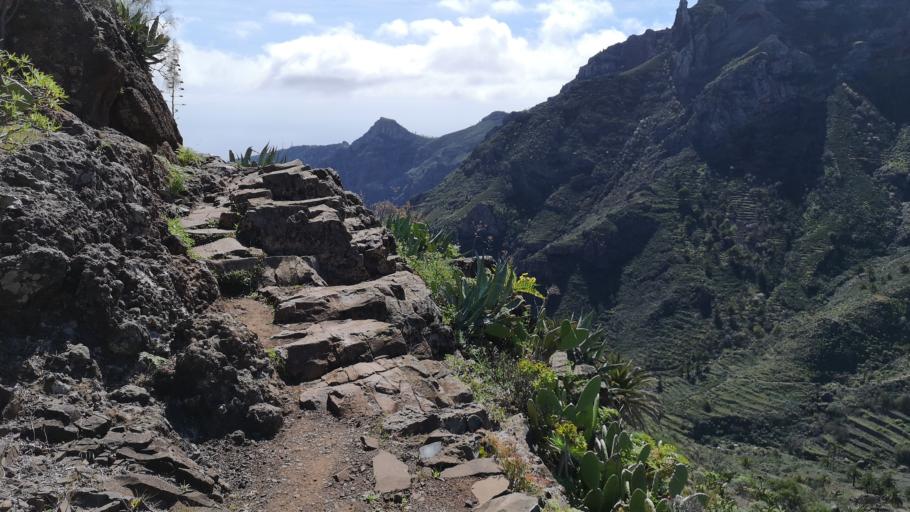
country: ES
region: Canary Islands
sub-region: Provincia de Santa Cruz de Tenerife
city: Alajero
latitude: 28.0845
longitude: -17.2335
